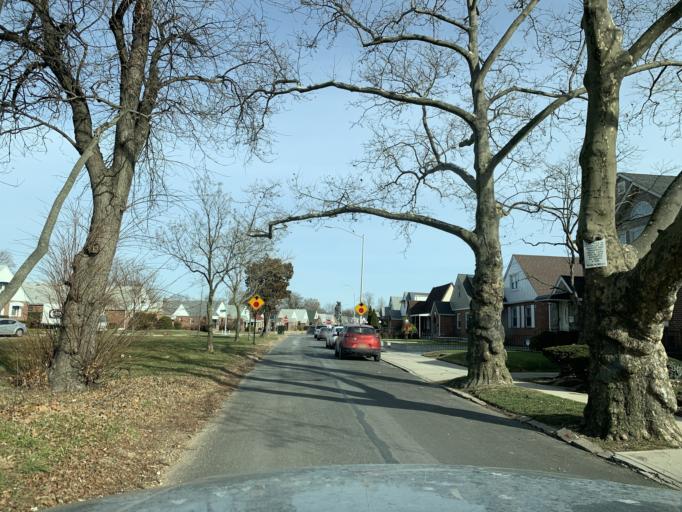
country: US
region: New York
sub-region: Queens County
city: Jamaica
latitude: 40.7014
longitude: -73.7705
